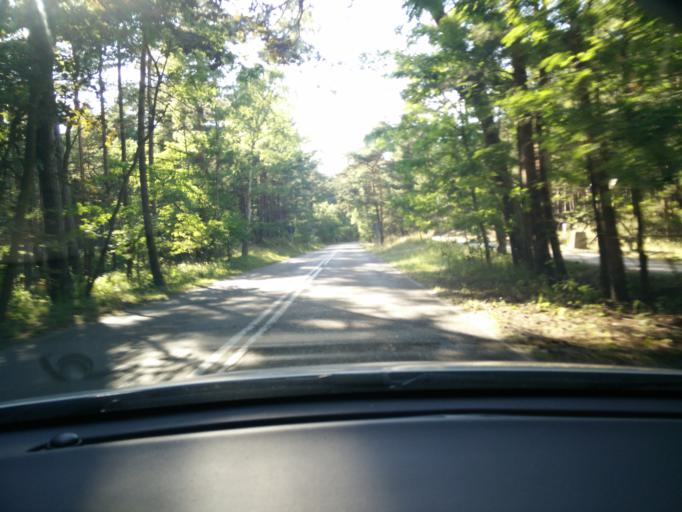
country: PL
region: Pomeranian Voivodeship
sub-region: Powiat pucki
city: Jastarnia
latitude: 54.6710
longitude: 18.7348
